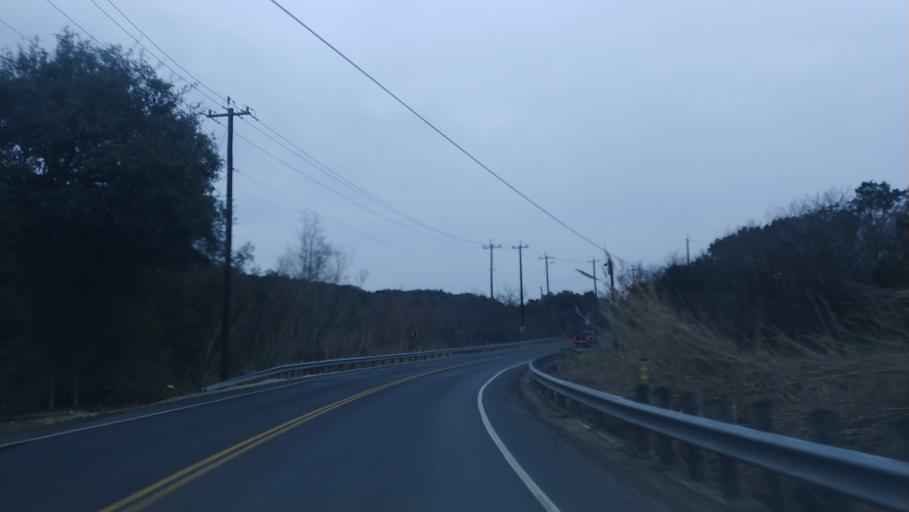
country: US
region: Texas
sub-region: Bexar County
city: Helotes
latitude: 29.6023
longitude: -98.6858
